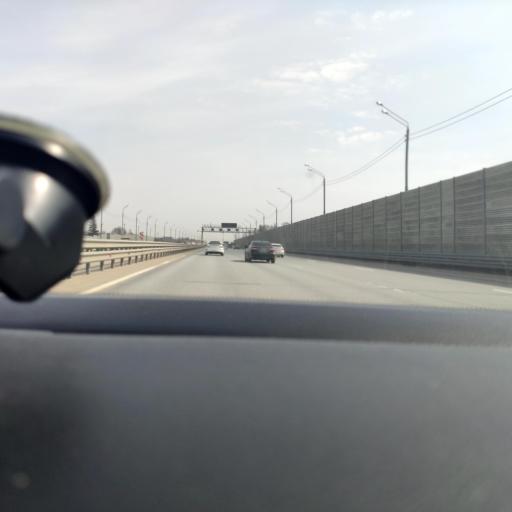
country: RU
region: Moskovskaya
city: Rozhdestveno
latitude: 55.8189
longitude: 36.9975
